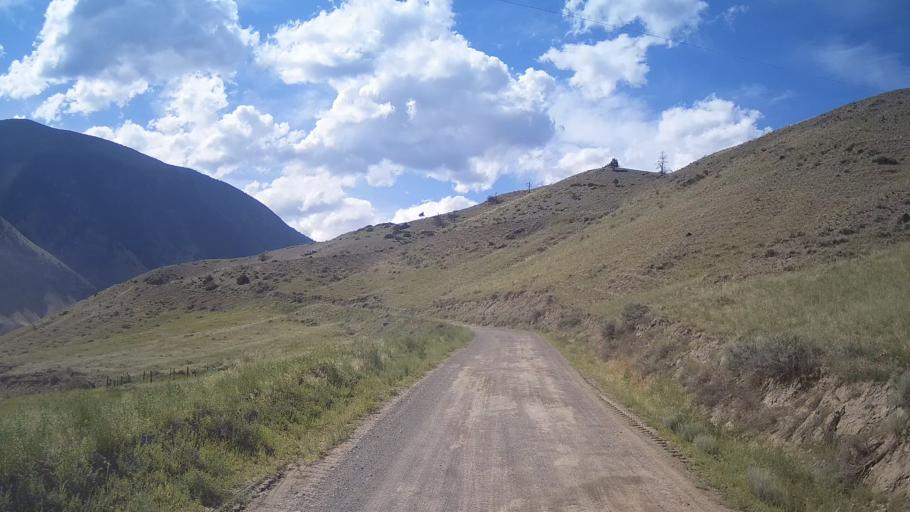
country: CA
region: British Columbia
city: Lillooet
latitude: 51.1821
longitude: -122.1153
